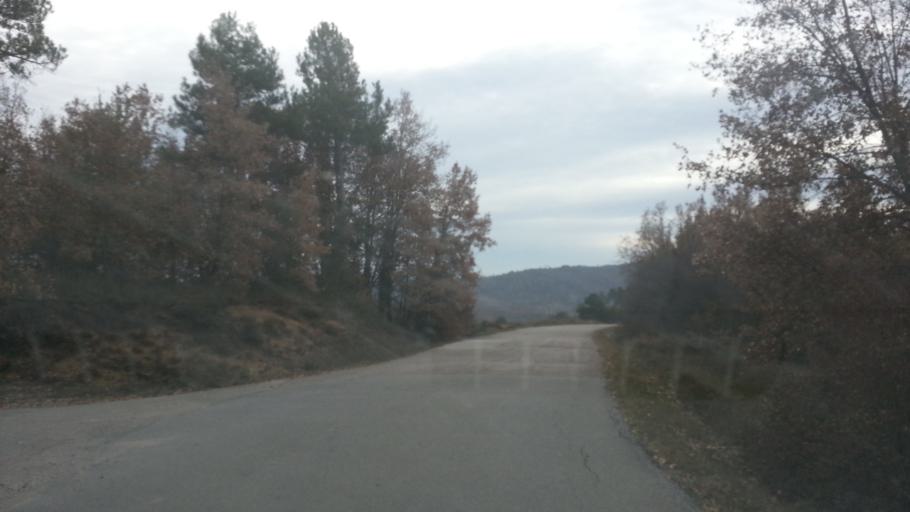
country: ES
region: Catalonia
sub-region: Provincia de Barcelona
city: Capolat
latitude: 41.9937
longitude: 1.7637
